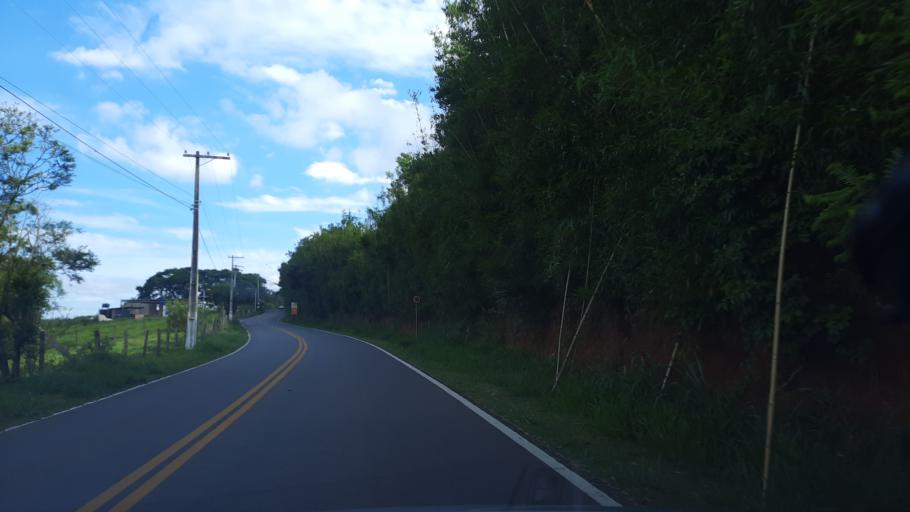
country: BR
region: Sao Paulo
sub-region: Atibaia
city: Atibaia
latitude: -23.0912
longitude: -46.5115
